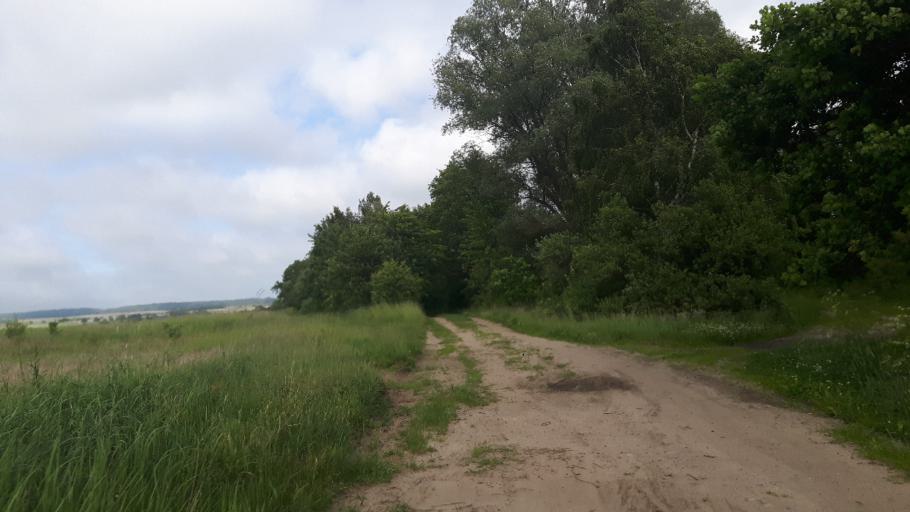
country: PL
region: Pomeranian Voivodeship
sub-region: Powiat slupski
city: Ustka
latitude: 54.5901
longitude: 16.9608
